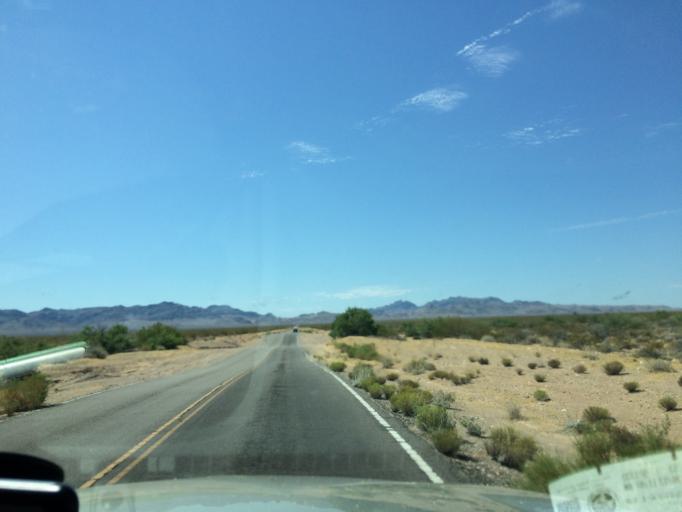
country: US
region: Nevada
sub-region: Clark County
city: Moapa Town
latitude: 36.4677
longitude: -114.7395
